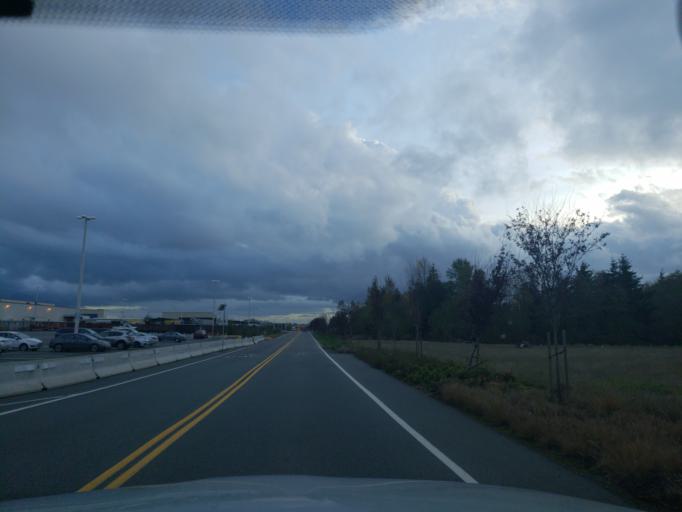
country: US
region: Washington
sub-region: Snohomish County
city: Mukilteo
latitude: 47.9309
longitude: -122.2847
